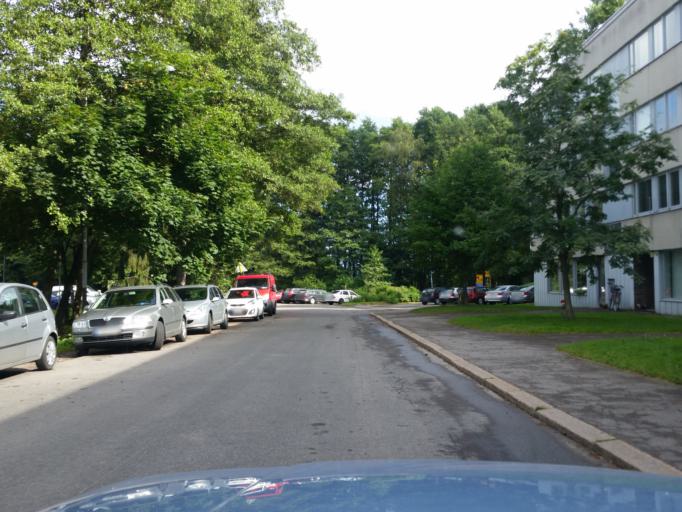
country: FI
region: Uusimaa
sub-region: Helsinki
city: Otaniemi
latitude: 60.1727
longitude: 24.8116
